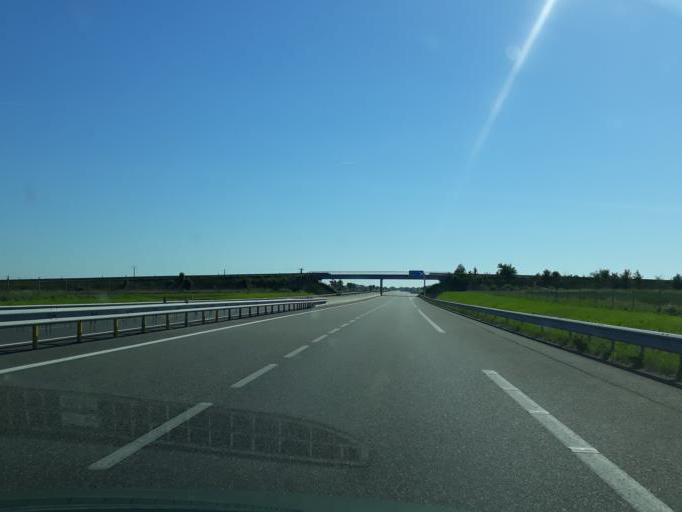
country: FR
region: Centre
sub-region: Departement du Loiret
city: Cepoy
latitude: 48.0562
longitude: 2.7246
